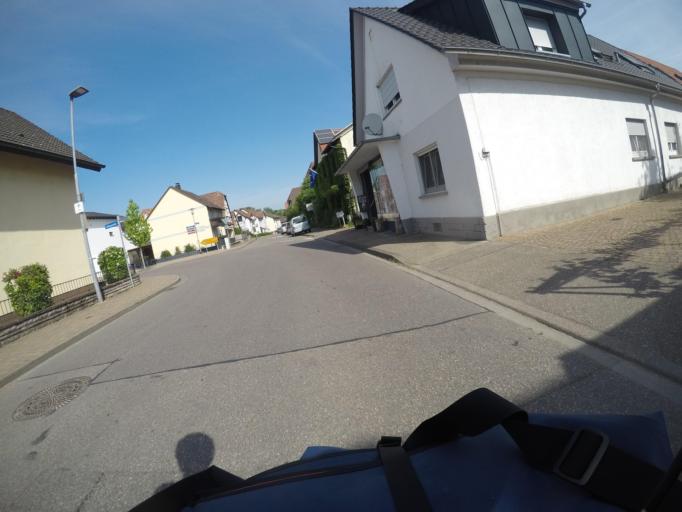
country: DE
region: Baden-Wuerttemberg
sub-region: Karlsruhe Region
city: Otigheim
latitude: 48.8934
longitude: 8.2327
